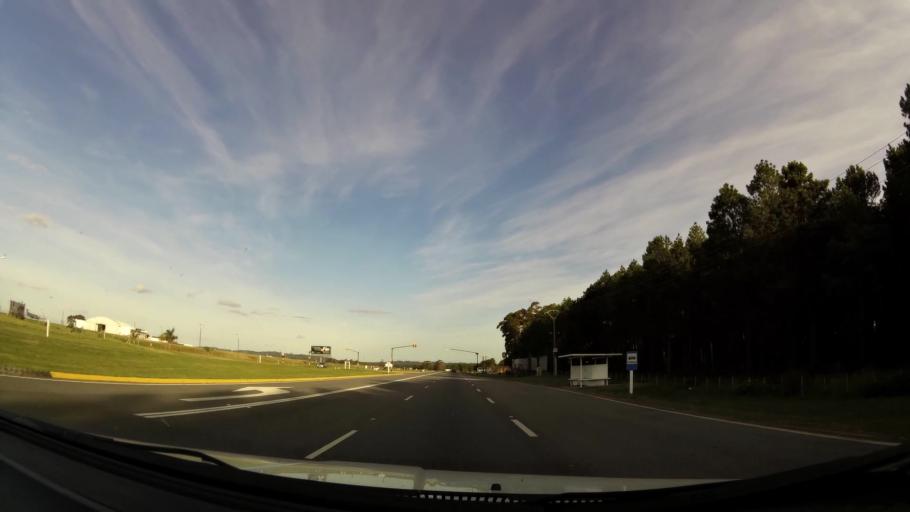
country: UY
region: Maldonado
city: Maldonado
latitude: -34.8654
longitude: -55.1000
